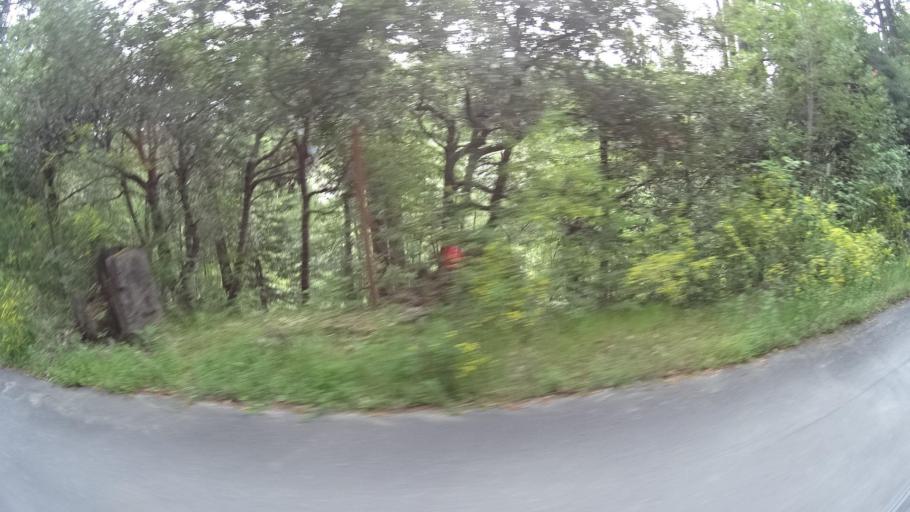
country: US
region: California
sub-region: Humboldt County
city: Redway
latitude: 40.2440
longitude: -123.8332
